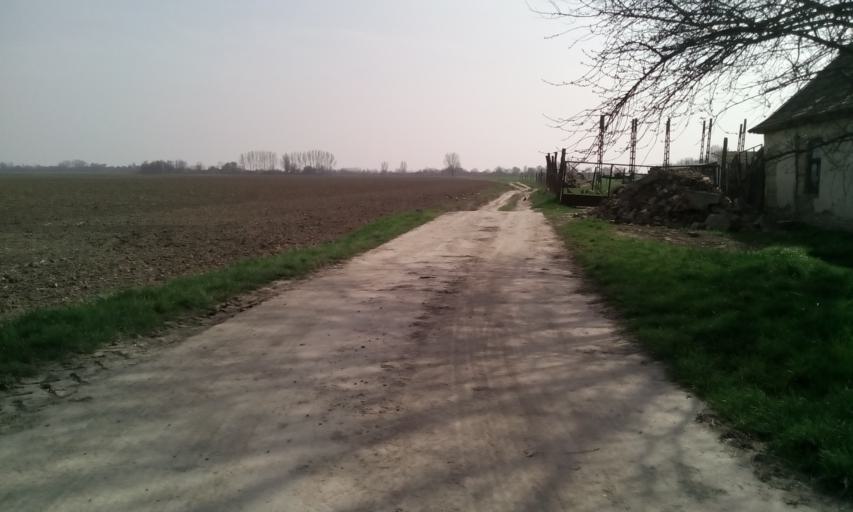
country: HU
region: Tolna
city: Decs
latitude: 46.2766
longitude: 18.7872
